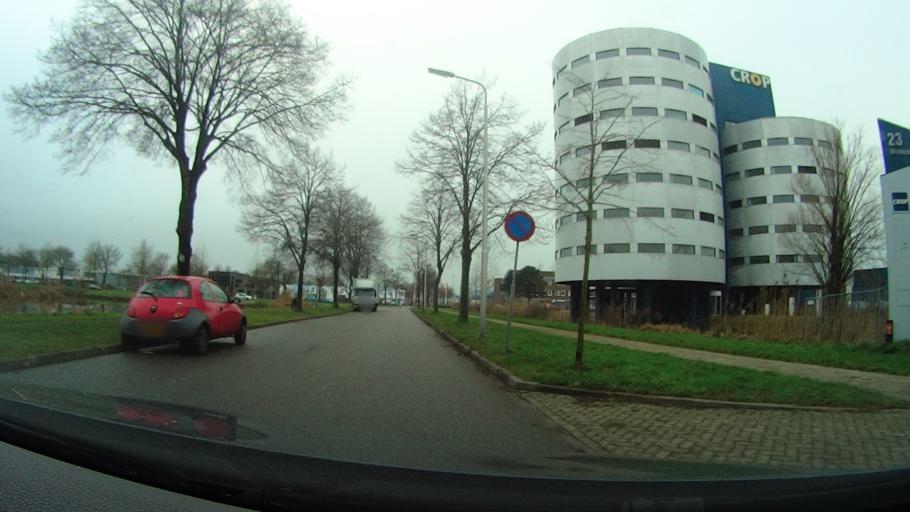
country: NL
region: Utrecht
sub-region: Gemeente Amersfoort
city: Hoogland
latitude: 52.1674
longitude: 5.3540
